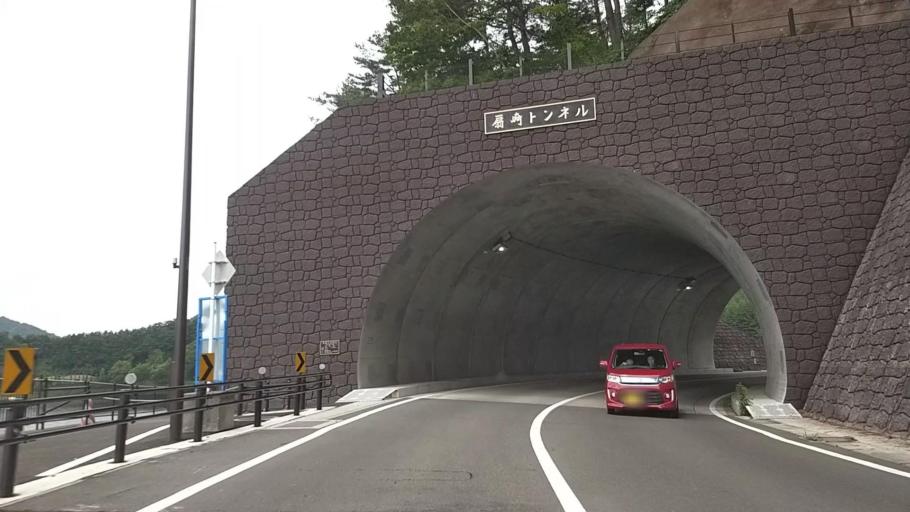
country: JP
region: Yamanashi
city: Fujikawaguchiko
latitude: 35.5127
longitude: 138.7329
